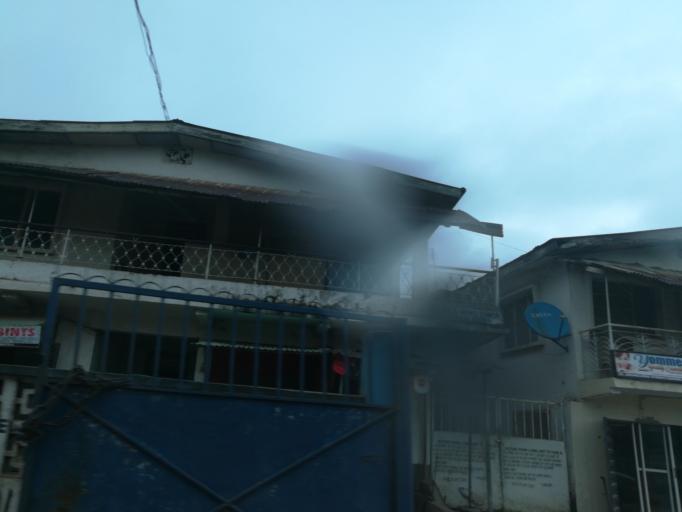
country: NG
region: Lagos
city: Oshodi
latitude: 6.5643
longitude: 3.3421
